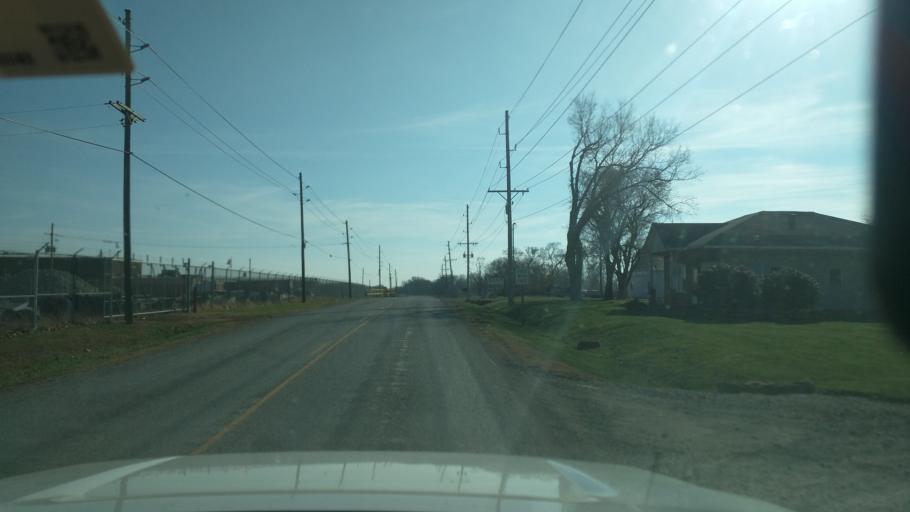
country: US
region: Kansas
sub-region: Lyon County
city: Emporia
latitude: 38.3935
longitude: -96.2080
